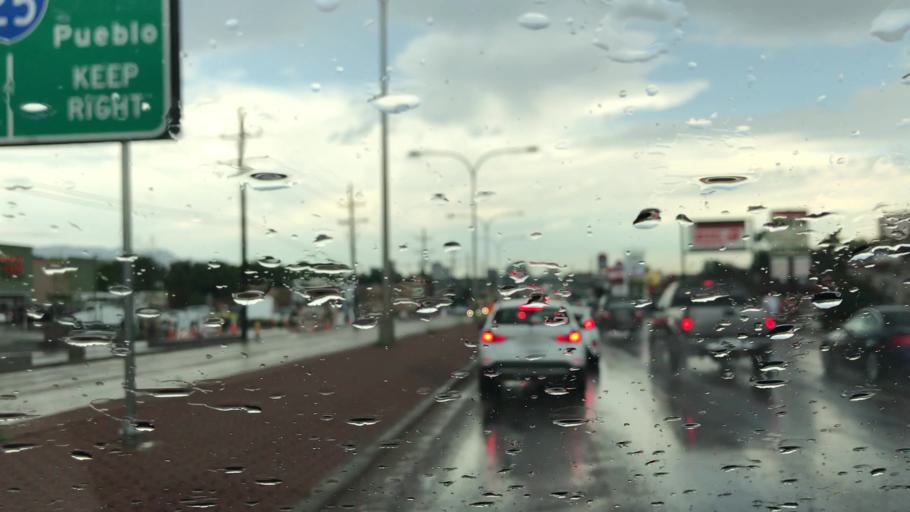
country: US
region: Colorado
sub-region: El Paso County
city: Colorado Springs
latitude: 38.8102
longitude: -104.8223
